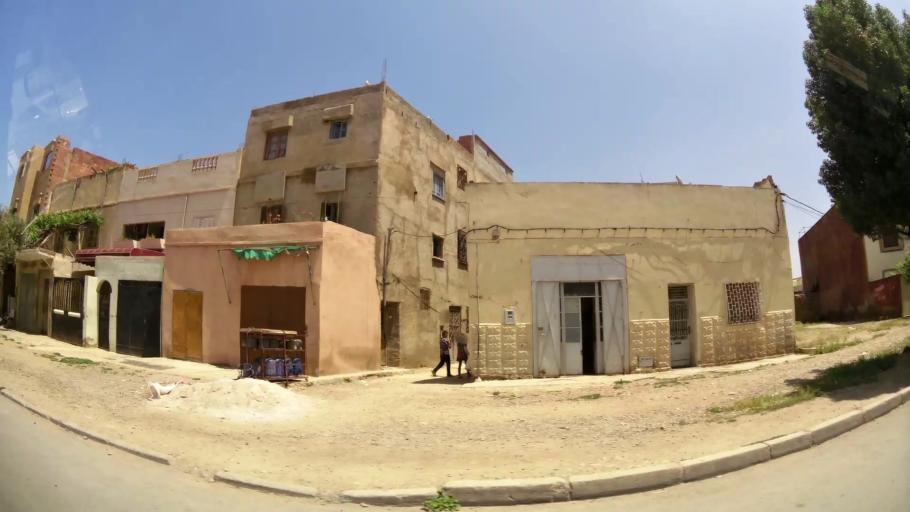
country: MA
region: Oriental
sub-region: Oujda-Angad
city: Oujda
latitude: 34.6906
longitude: -1.8918
